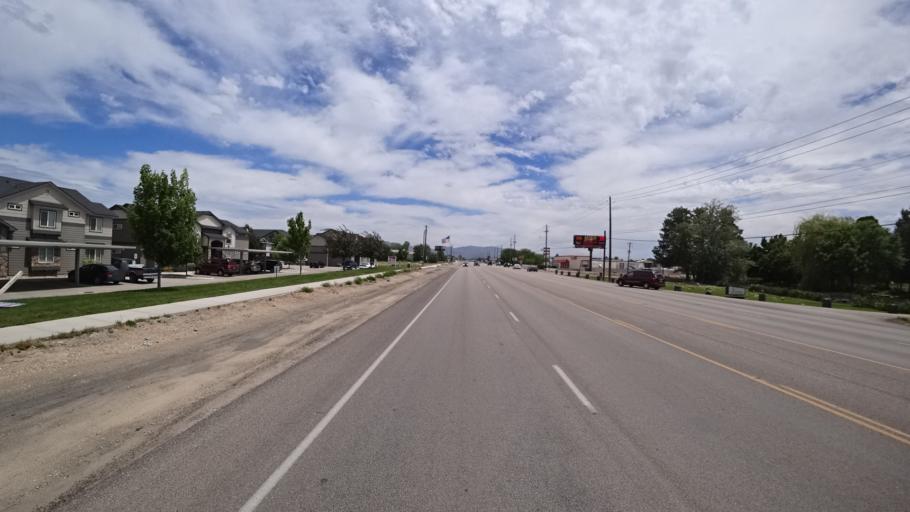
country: US
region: Idaho
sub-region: Ada County
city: Meridian
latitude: 43.6195
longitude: -116.3307
